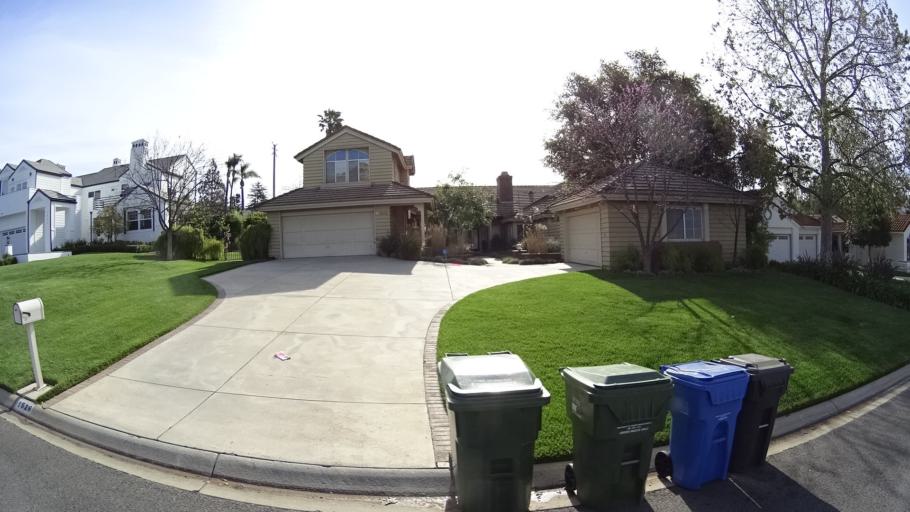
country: US
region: California
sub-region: Ventura County
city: Oak Park
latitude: 34.1914
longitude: -118.7859
